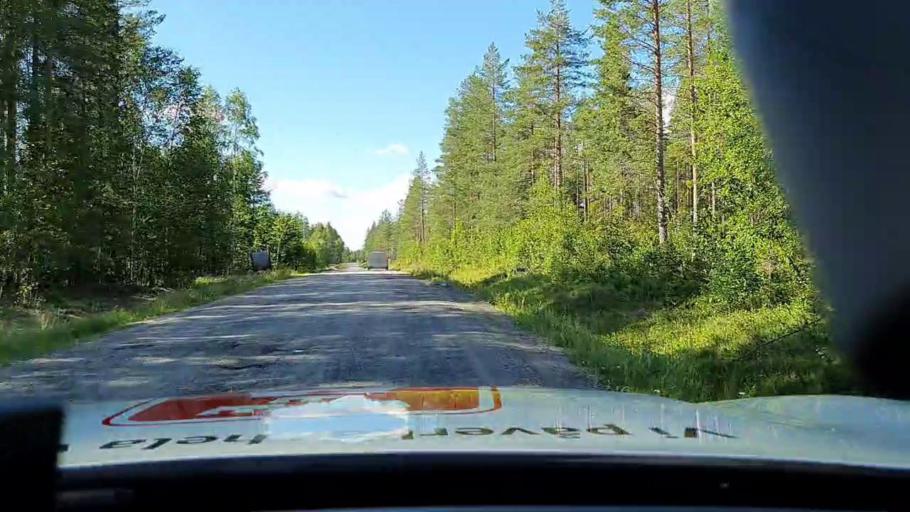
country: SE
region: Norrbotten
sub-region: Overkalix Kommun
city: OEverkalix
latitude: 66.2490
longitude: 23.1352
